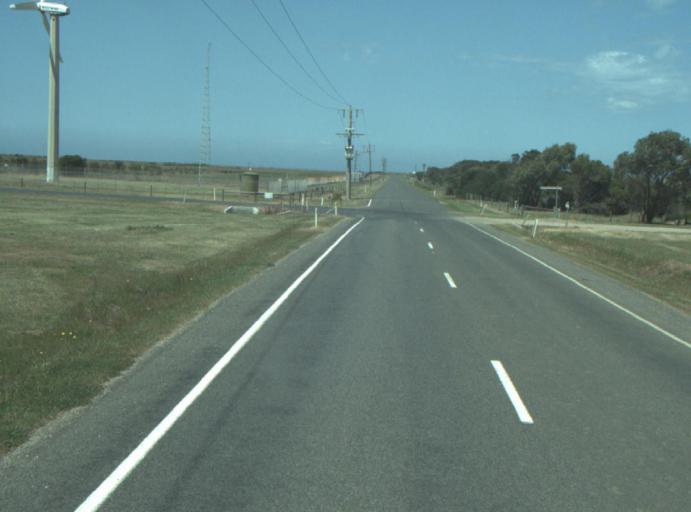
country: AU
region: Victoria
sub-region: Greater Geelong
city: Leopold
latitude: -38.2778
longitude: 144.4209
